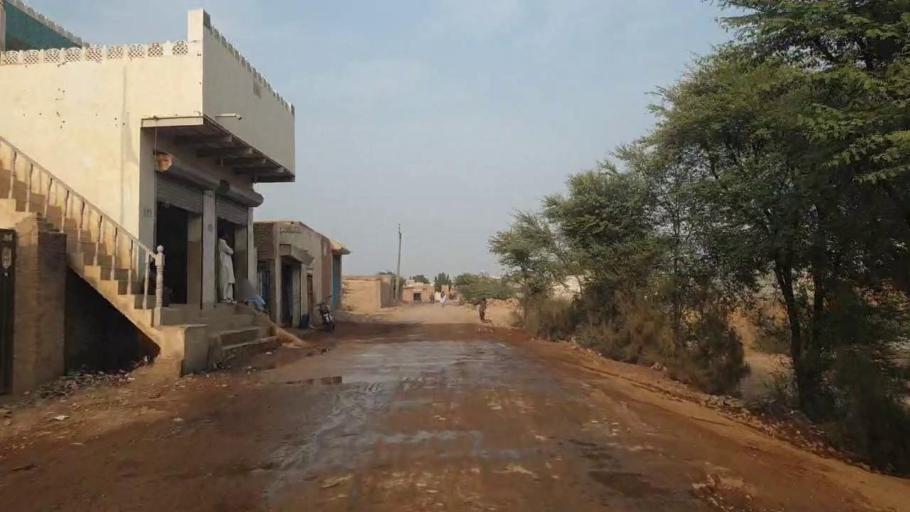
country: PK
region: Sindh
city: Sann
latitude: 26.1368
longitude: 68.0504
